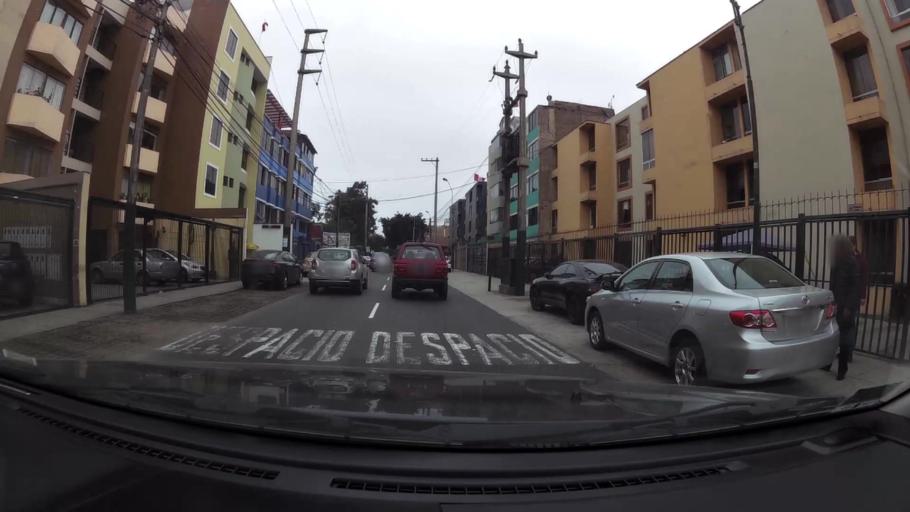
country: PE
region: Lima
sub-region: Lima
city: Surco
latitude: -12.1427
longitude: -77.0037
